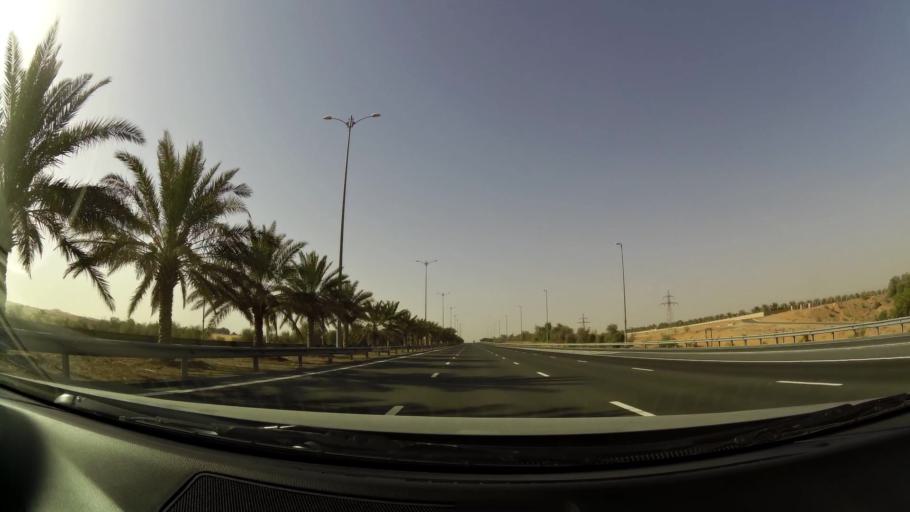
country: OM
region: Al Buraimi
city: Al Buraymi
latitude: 24.5449
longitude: 55.7559
